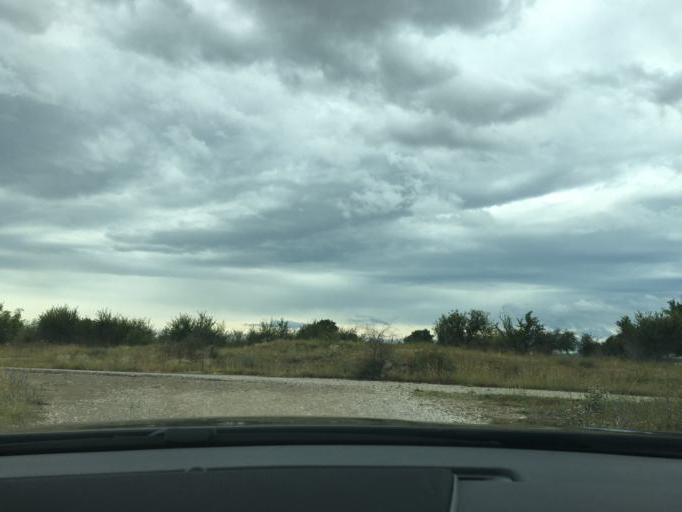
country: MK
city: Klechovce
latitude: 42.1566
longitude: 21.9384
